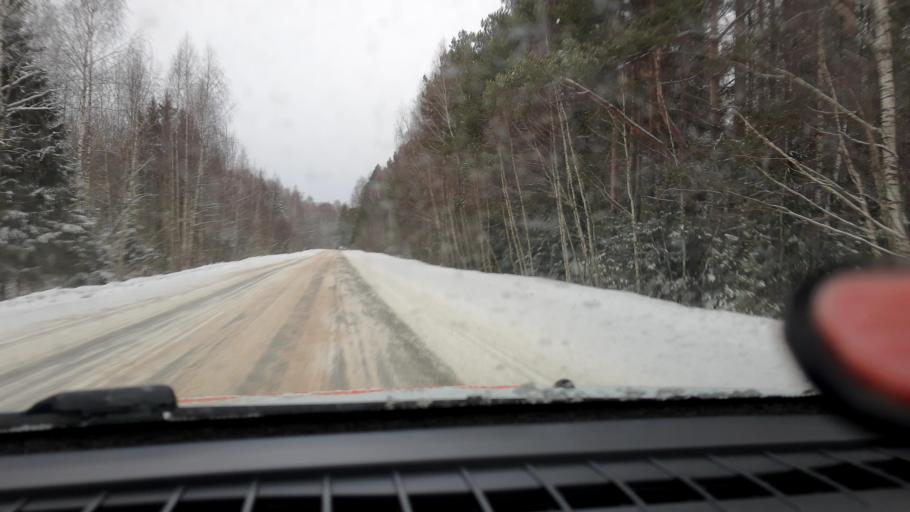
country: RU
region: Nizjnij Novgorod
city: Pamyat' Parizhskoy Kommuny
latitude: 56.2600
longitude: 44.4516
